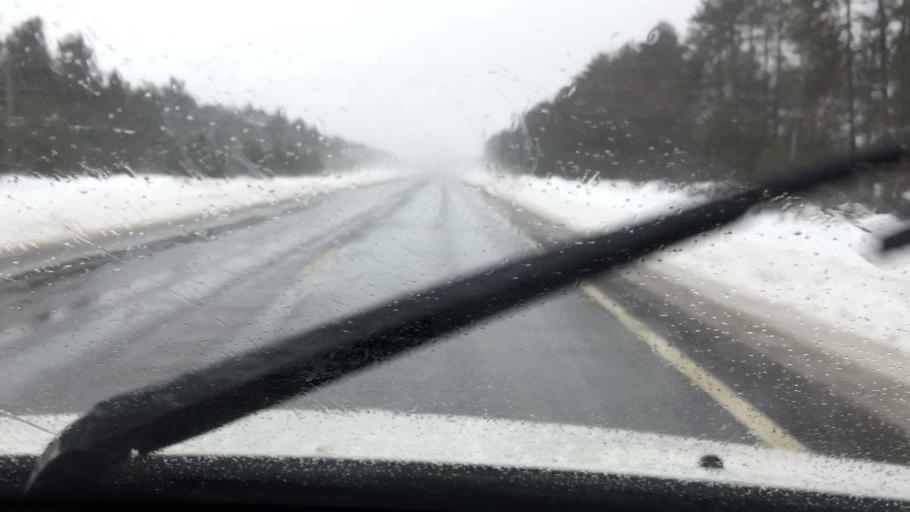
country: US
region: Michigan
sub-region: Antrim County
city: Mancelona
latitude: 44.9250
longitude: -85.0509
